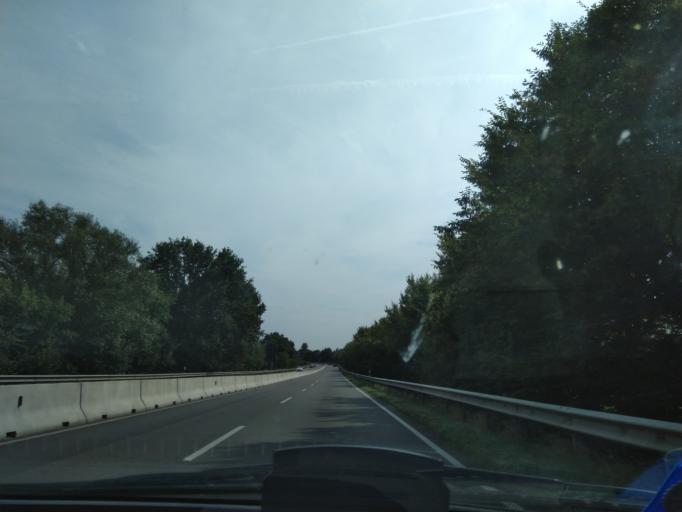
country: DE
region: Lower Saxony
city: Meppen
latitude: 52.6893
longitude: 7.2829
